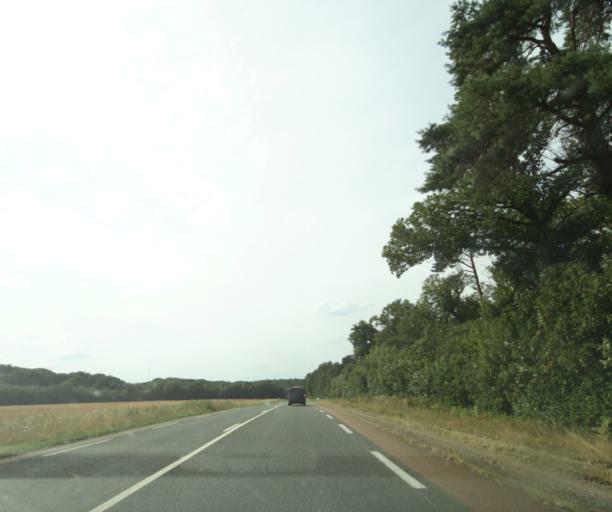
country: FR
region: Pays de la Loire
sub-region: Departement de la Sarthe
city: Luceau
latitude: 47.7530
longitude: 0.3660
